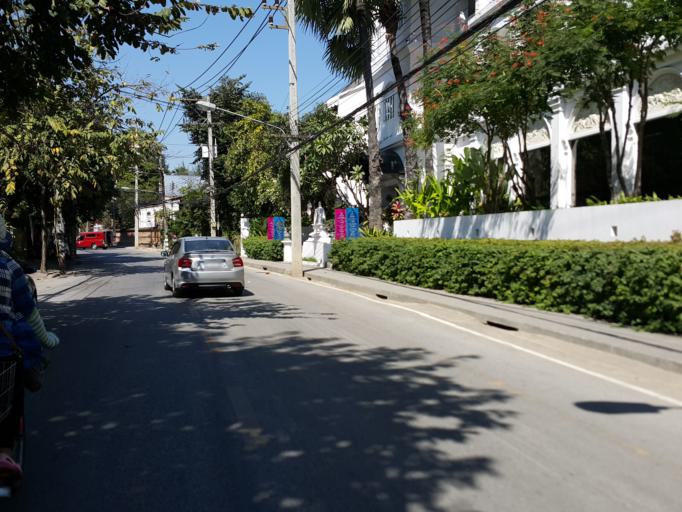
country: TH
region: Chiang Mai
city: Chiang Mai
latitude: 18.7794
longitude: 99.0046
